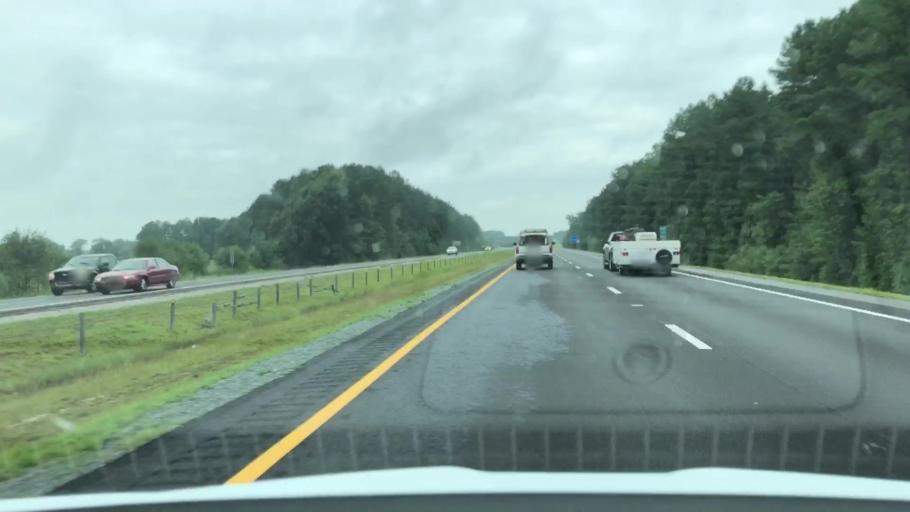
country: US
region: North Carolina
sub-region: Wayne County
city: Fremont
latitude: 35.4847
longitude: -77.9912
